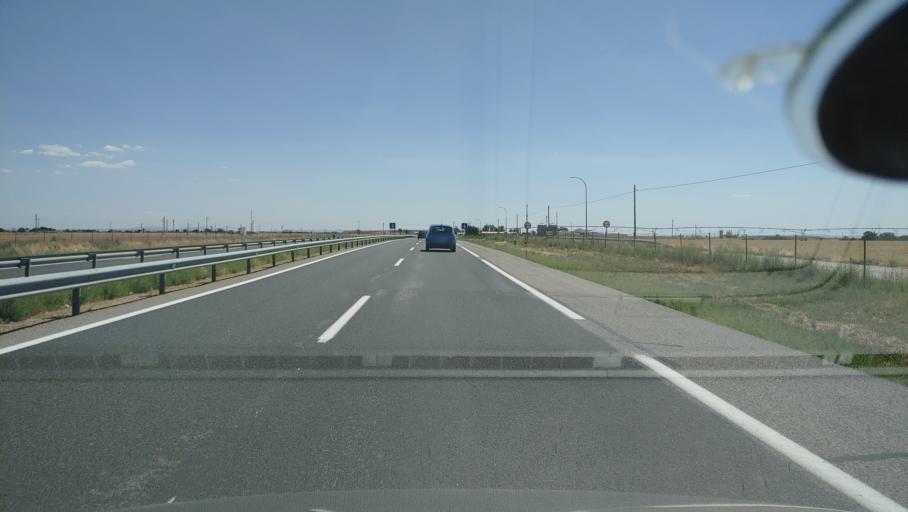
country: ES
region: Castille-La Mancha
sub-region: Provincia de Ciudad Real
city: Villarta de San Juan
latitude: 39.1773
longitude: -3.3971
